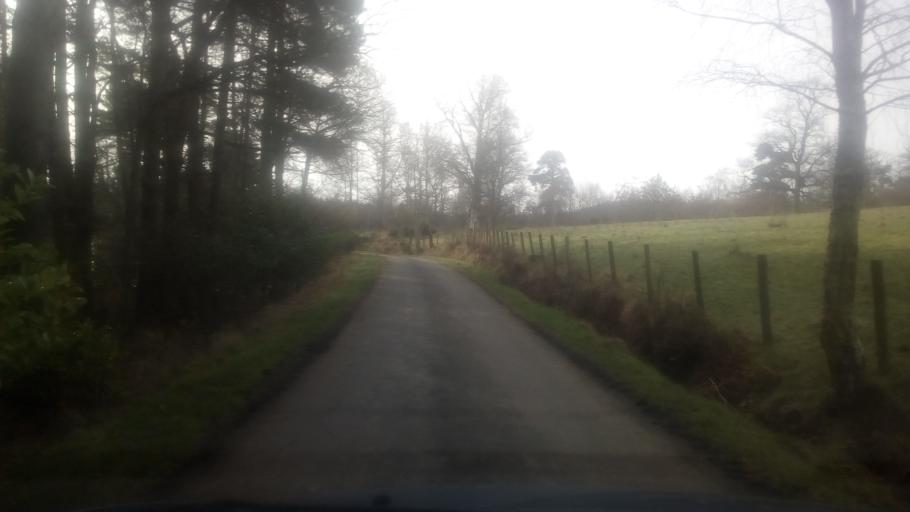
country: GB
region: Scotland
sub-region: The Scottish Borders
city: Jedburgh
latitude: 55.4389
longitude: -2.6407
